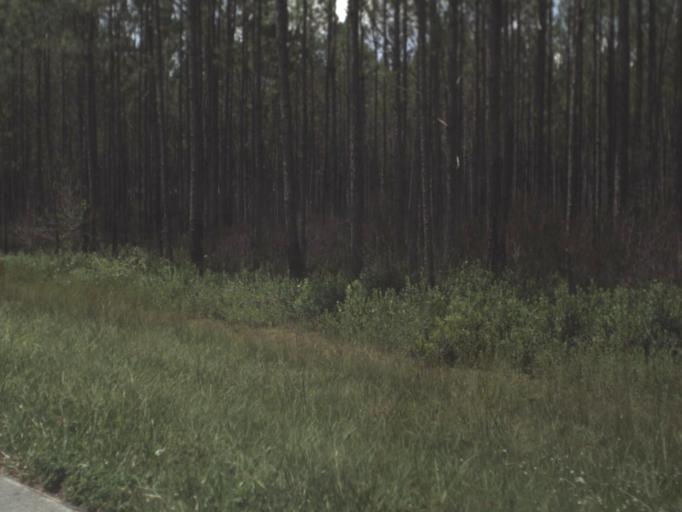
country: US
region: Florida
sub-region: Columbia County
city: Five Points
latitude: 30.5707
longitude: -82.4518
